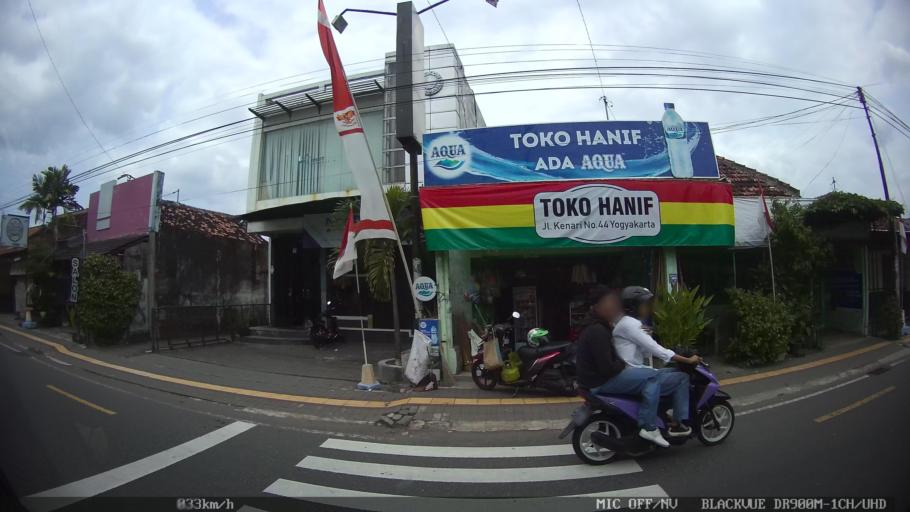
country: ID
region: Daerah Istimewa Yogyakarta
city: Yogyakarta
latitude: -7.7988
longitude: 110.3893
